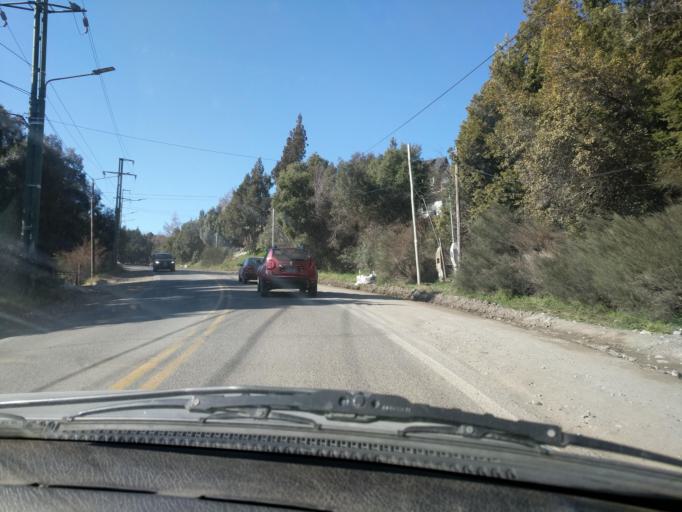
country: AR
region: Rio Negro
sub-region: Departamento de Bariloche
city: San Carlos de Bariloche
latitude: -41.1271
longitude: -71.3912
